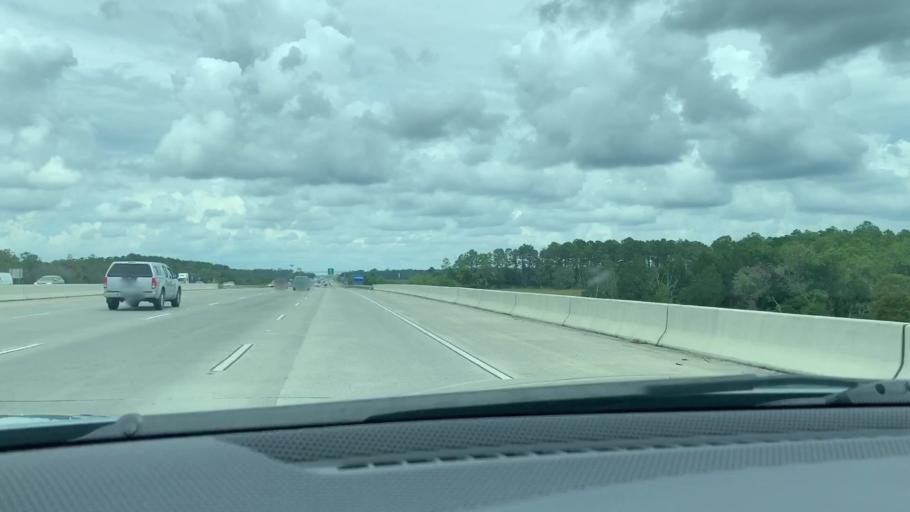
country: US
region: Georgia
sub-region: McIntosh County
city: Darien
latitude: 31.3731
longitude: -81.4549
